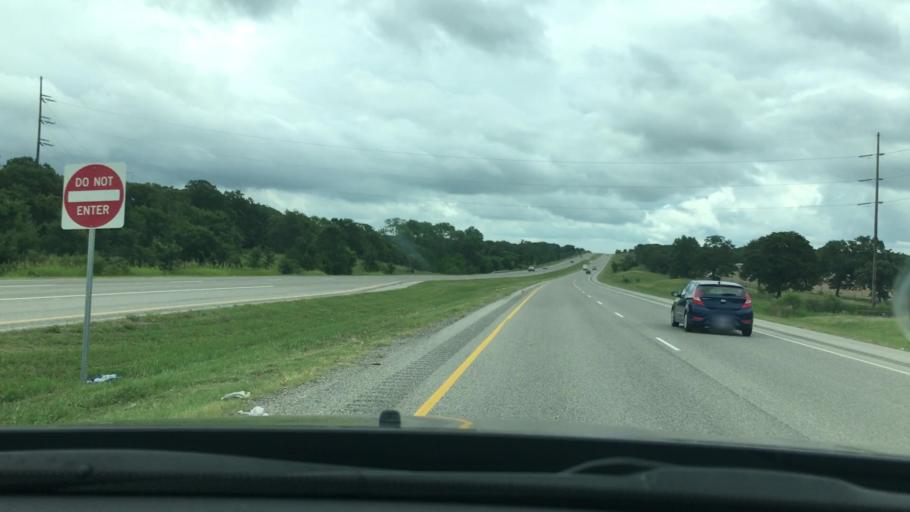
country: US
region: Oklahoma
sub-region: Carter County
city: Ardmore
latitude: 34.1323
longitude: -97.0903
